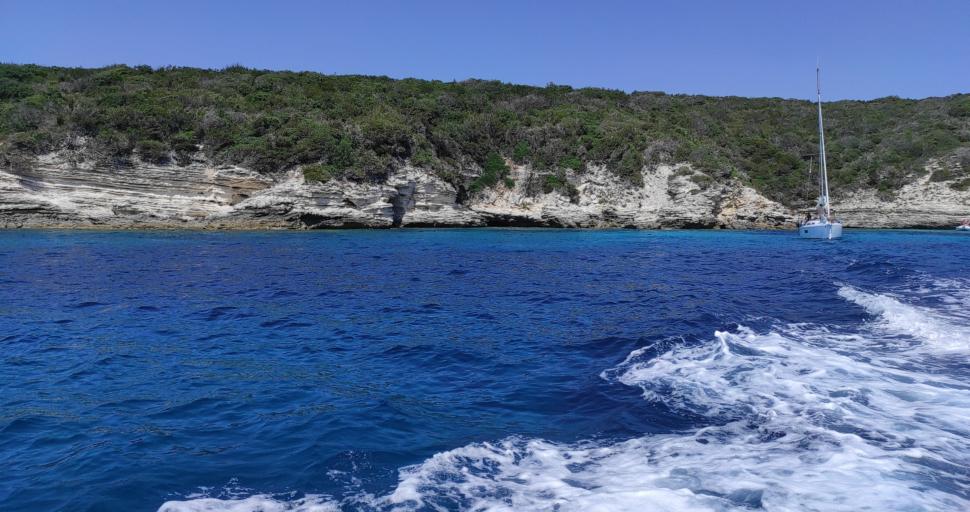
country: FR
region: Corsica
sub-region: Departement de la Corse-du-Sud
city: Bonifacio
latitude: 41.3935
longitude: 9.1333
